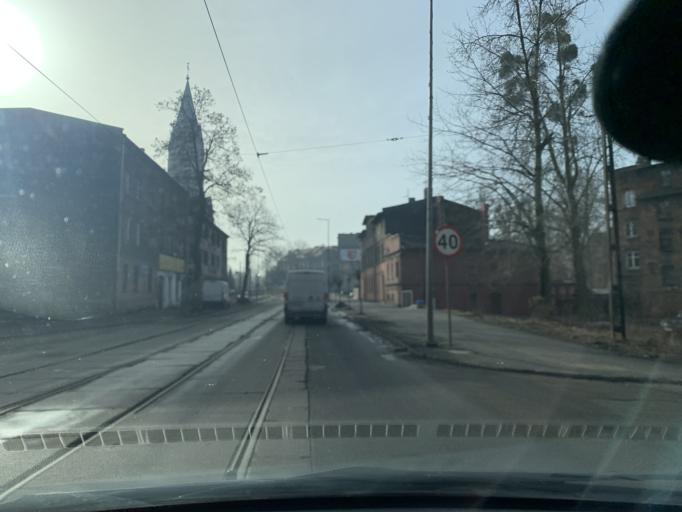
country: PL
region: Silesian Voivodeship
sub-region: Swietochlowice
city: Swietochlowice
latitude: 50.3368
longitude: 18.8692
